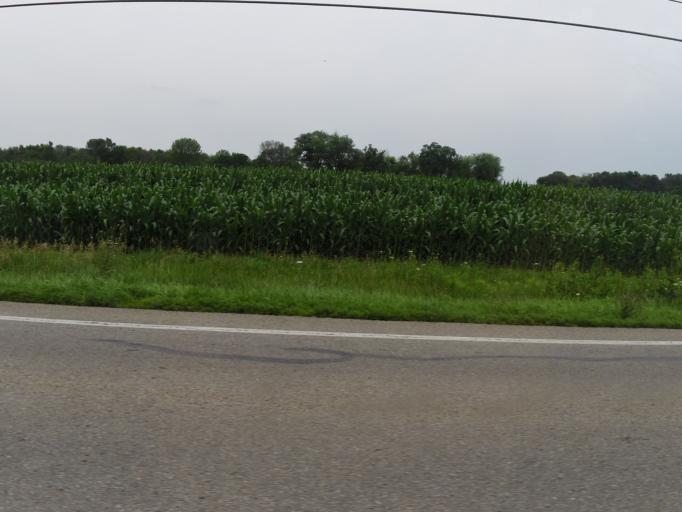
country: US
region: Ohio
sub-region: Clinton County
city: Wilmington
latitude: 39.4755
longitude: -83.8929
